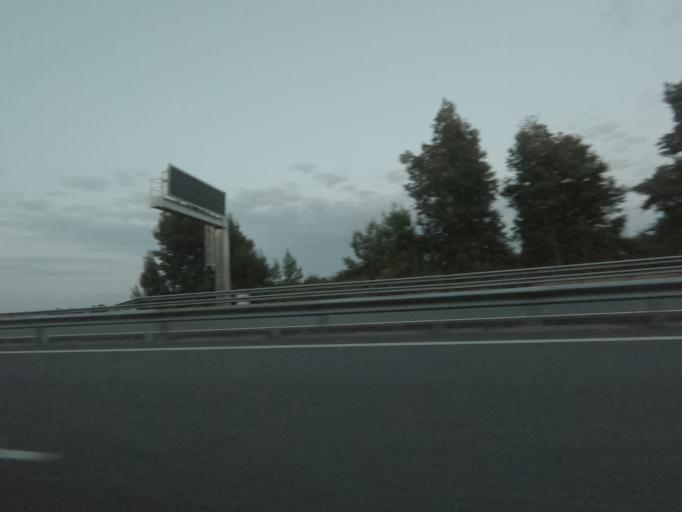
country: ES
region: Galicia
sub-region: Provincia de Pontevedra
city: Tui
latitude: 42.0595
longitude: -8.6508
